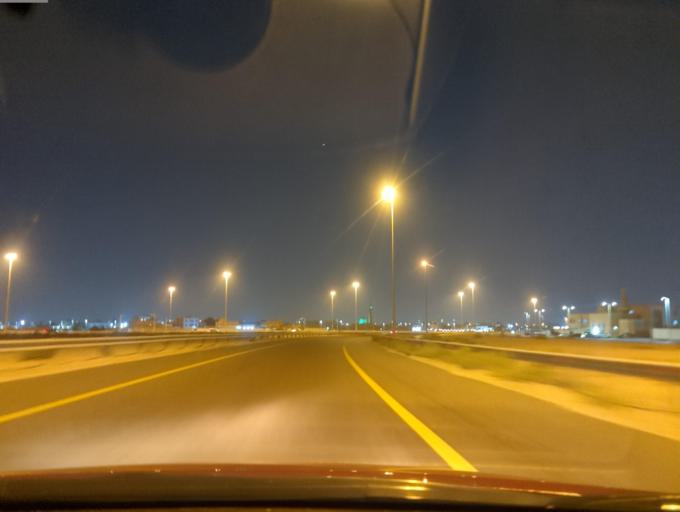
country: AE
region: Abu Dhabi
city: Abu Dhabi
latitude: 24.3803
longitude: 54.7323
